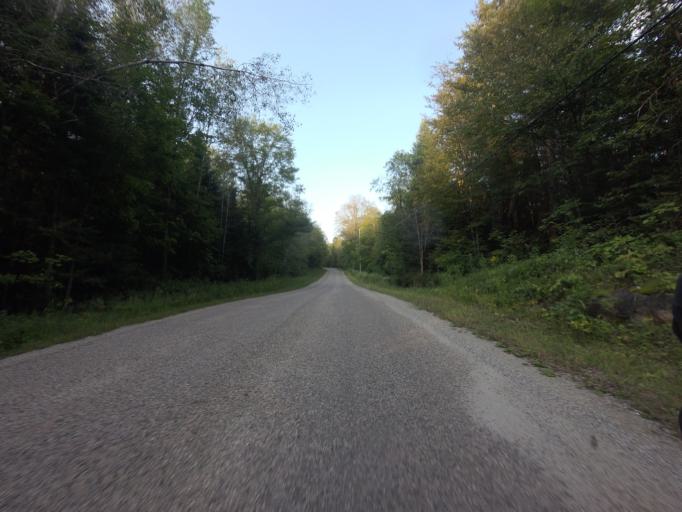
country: CA
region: Ontario
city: Renfrew
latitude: 45.0232
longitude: -76.7537
